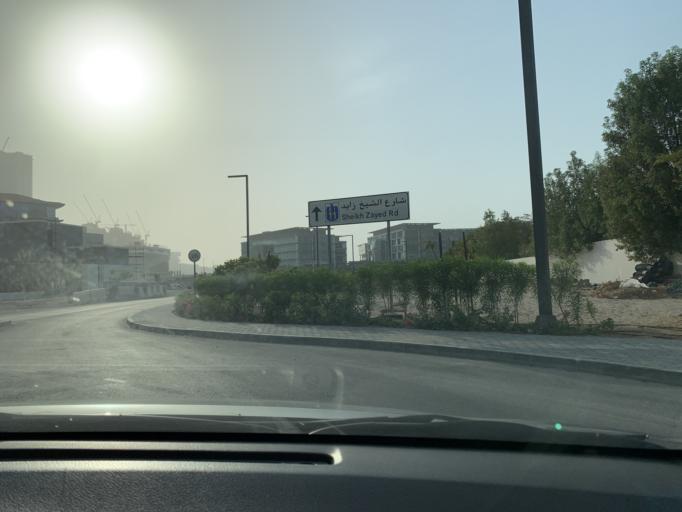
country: AE
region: Dubai
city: Dubai
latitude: 25.0982
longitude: 55.1658
